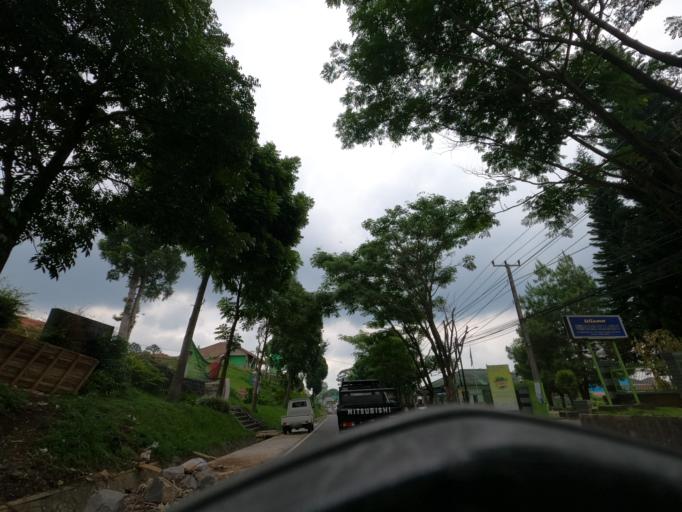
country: ID
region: West Java
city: Sukabumi
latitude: -6.7529
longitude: 107.0467
